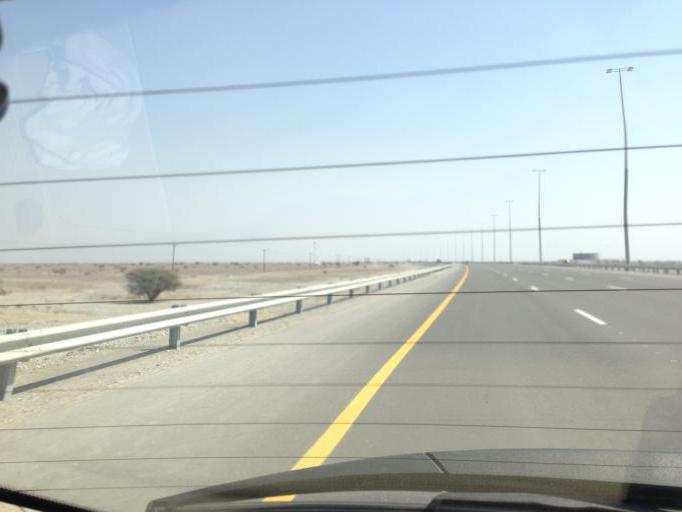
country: OM
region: Al Batinah
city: Barka'
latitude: 23.5798
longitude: 57.7889
